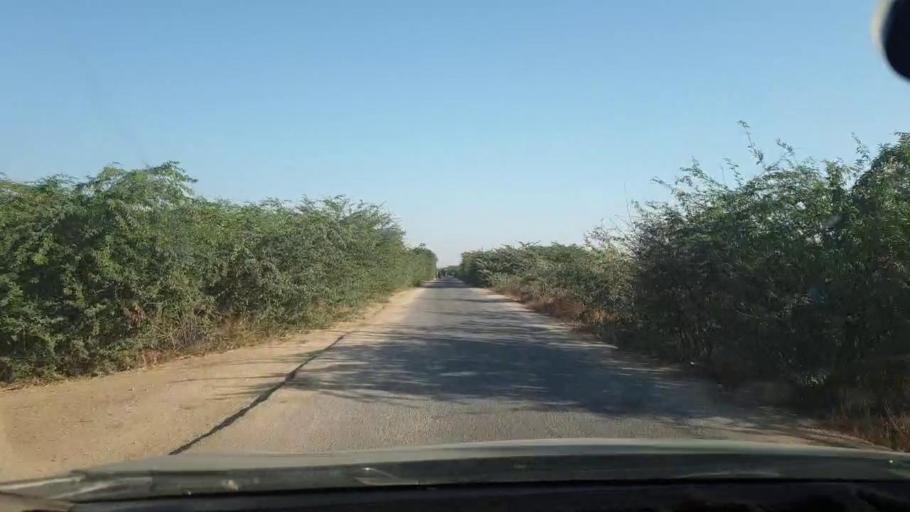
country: PK
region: Sindh
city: Malir Cantonment
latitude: 25.1479
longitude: 67.1882
